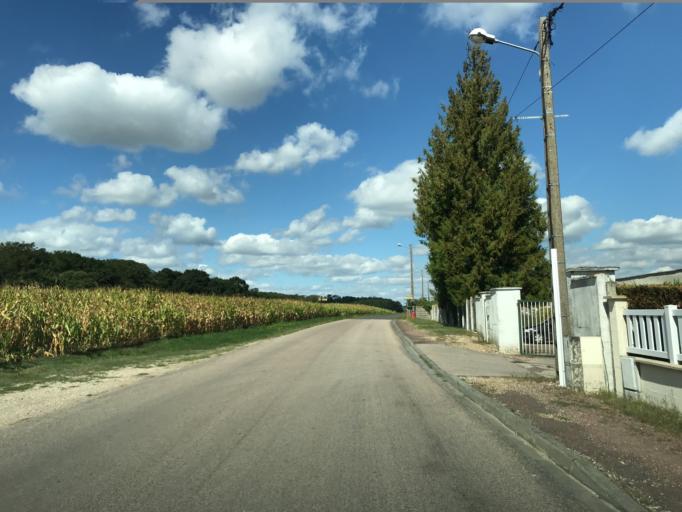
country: FR
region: Haute-Normandie
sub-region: Departement de l'Eure
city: Saint-Just
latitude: 49.1447
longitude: 1.4121
